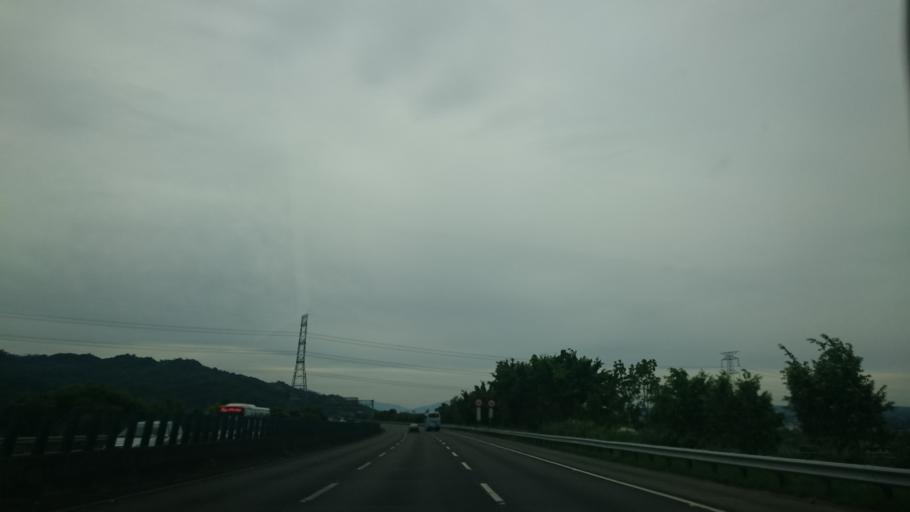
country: TW
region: Taiwan
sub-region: Nantou
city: Nantou
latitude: 23.8904
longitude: 120.7104
